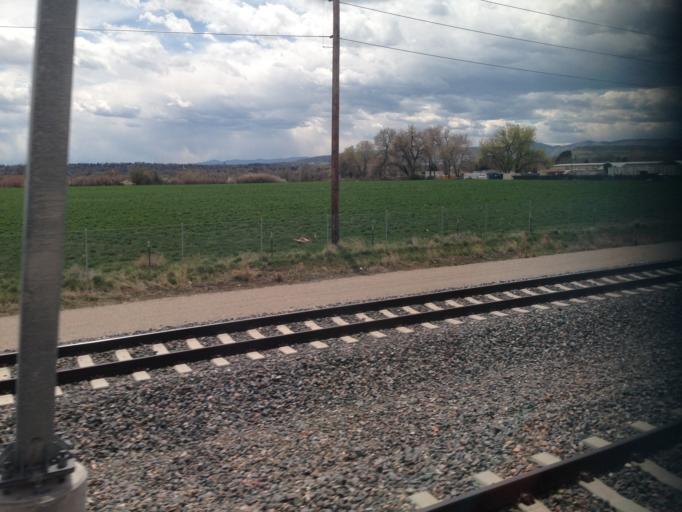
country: US
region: Colorado
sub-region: Jefferson County
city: Arvada
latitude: 39.7893
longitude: -105.1272
